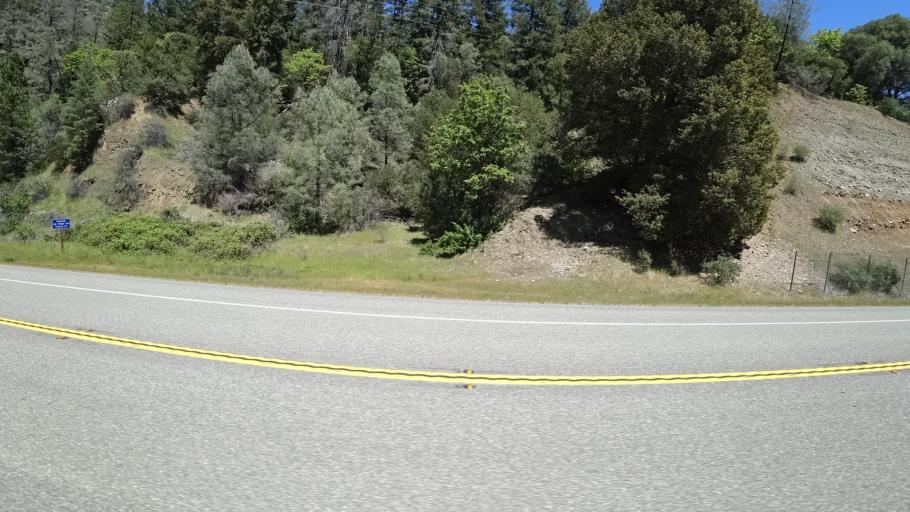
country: US
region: California
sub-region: Trinity County
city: Hayfork
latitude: 40.7367
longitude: -123.2339
